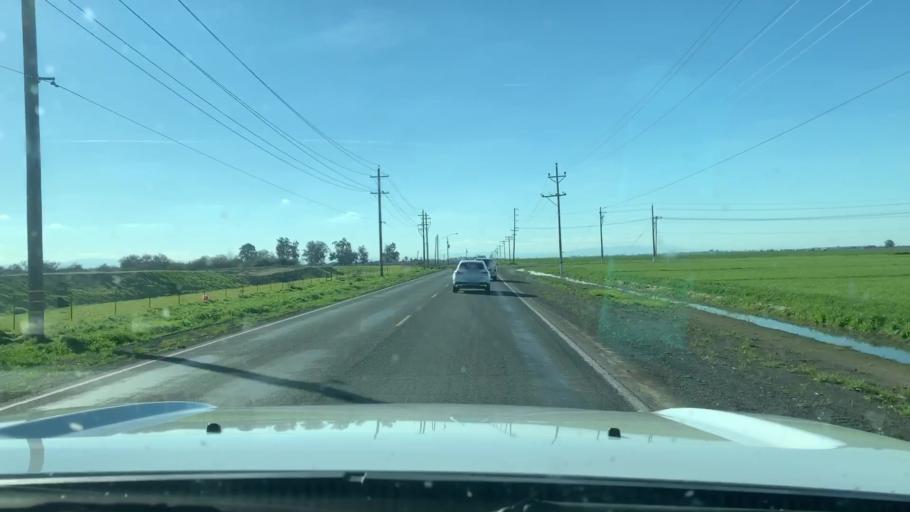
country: US
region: California
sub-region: Kings County
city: Home Garden
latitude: 36.2112
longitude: -119.6528
